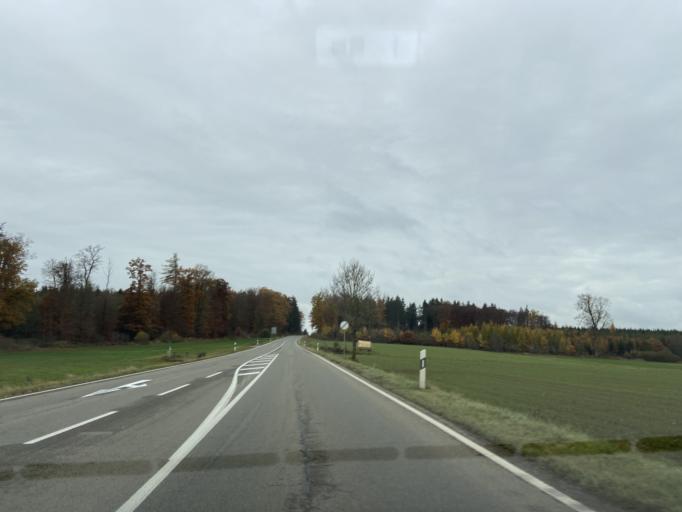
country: DE
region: Baden-Wuerttemberg
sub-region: Tuebingen Region
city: Wald
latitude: 47.9689
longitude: 9.1537
